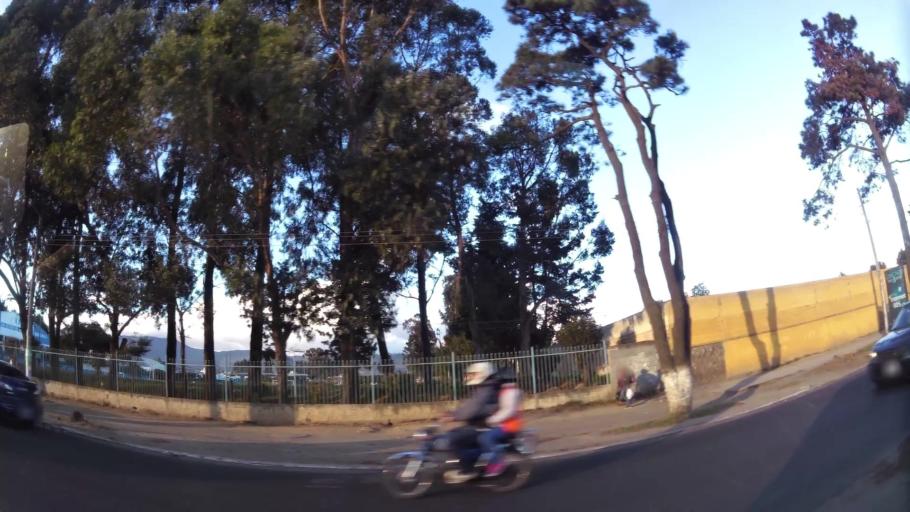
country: GT
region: Quetzaltenango
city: Quetzaltenango
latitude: 14.8456
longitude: -91.5296
